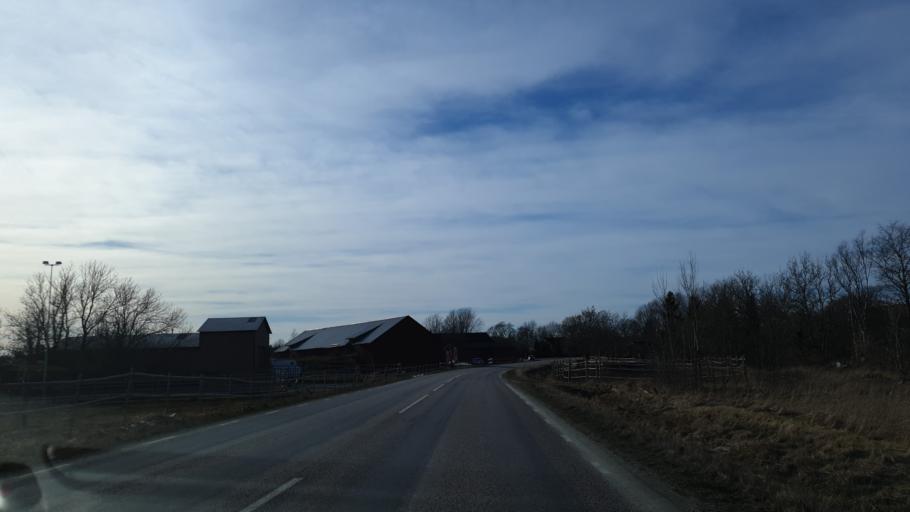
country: SE
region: Uppsala
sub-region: Enkopings Kommun
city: Grillby
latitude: 59.5940
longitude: 17.1823
